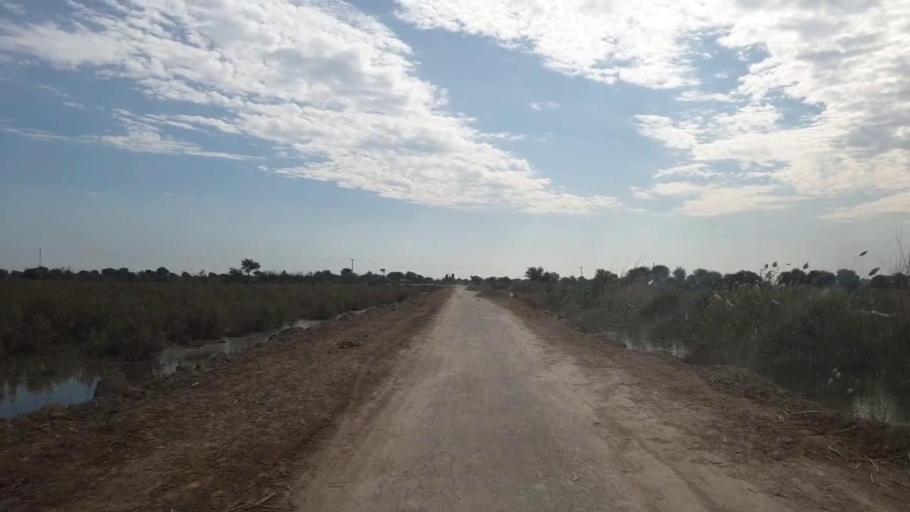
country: PK
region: Sindh
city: Jhol
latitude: 25.9975
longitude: 68.8962
